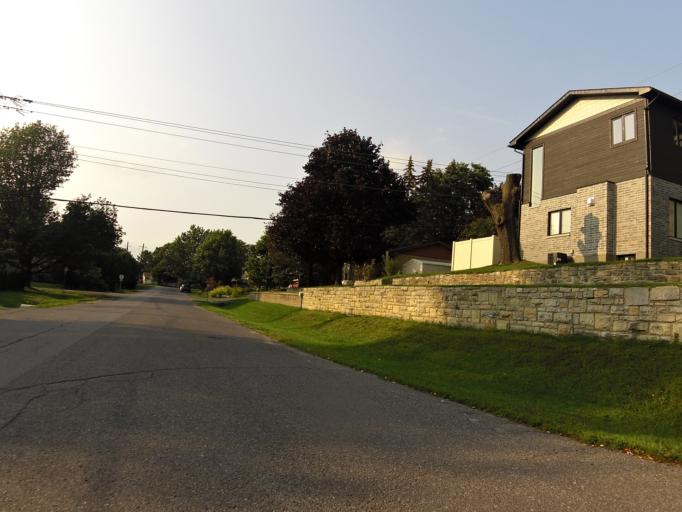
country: CA
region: Ontario
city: Ottawa
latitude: 45.3496
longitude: -75.7415
